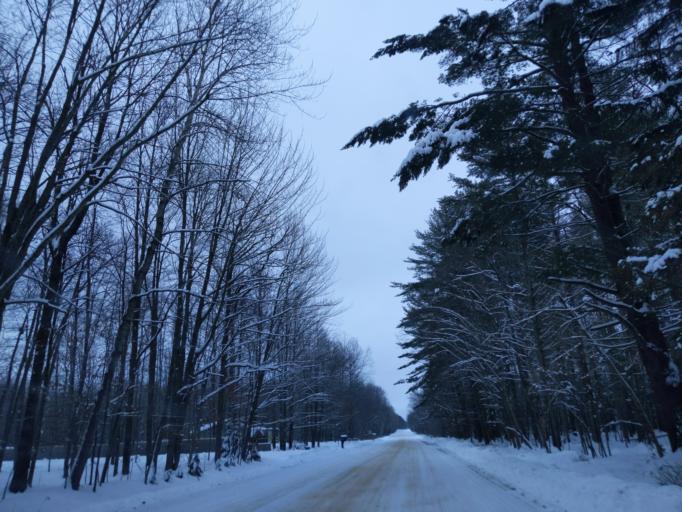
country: US
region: Wisconsin
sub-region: Marathon County
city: Marathon
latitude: 44.7718
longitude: -89.8673
